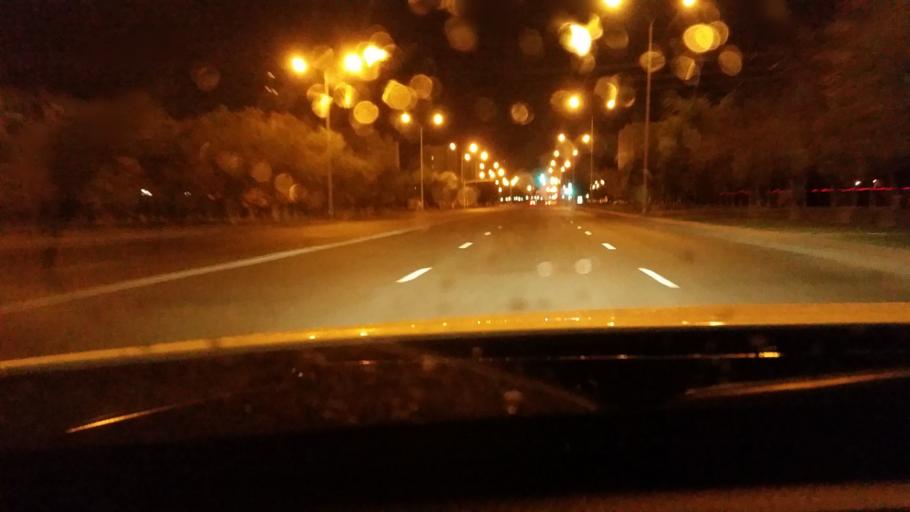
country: KZ
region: Astana Qalasy
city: Astana
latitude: 51.1533
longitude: 71.4800
